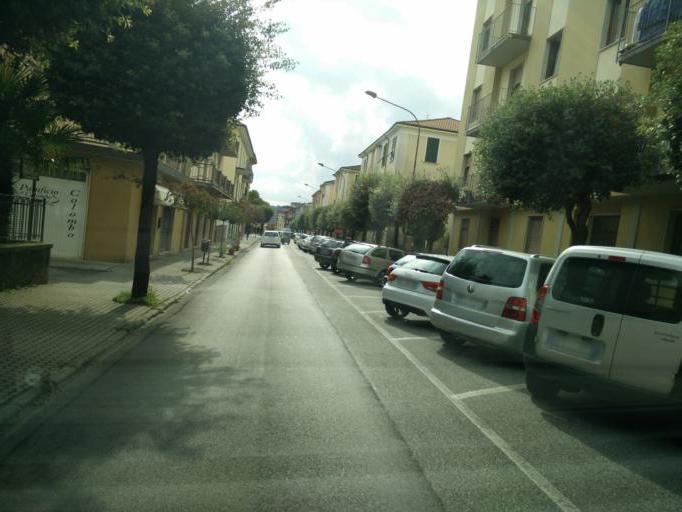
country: IT
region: Tuscany
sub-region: Provincia di Massa-Carrara
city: Pontremoli
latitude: 44.3767
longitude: 9.8795
